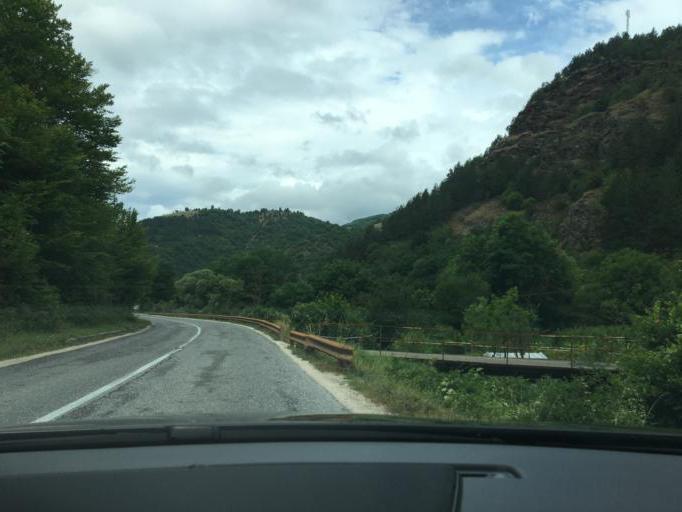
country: MK
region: Kriva Palanka
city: Kriva Palanka
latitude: 42.2305
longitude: 22.3704
